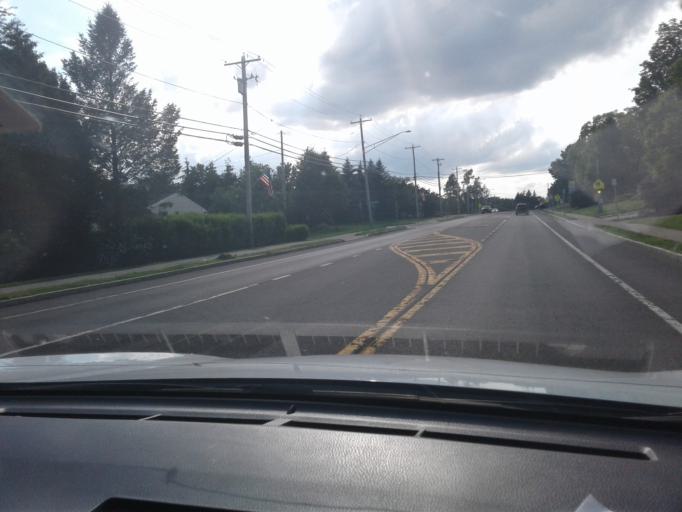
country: US
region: New York
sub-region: Onondaga County
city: East Syracuse
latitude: 43.0360
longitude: -76.0711
